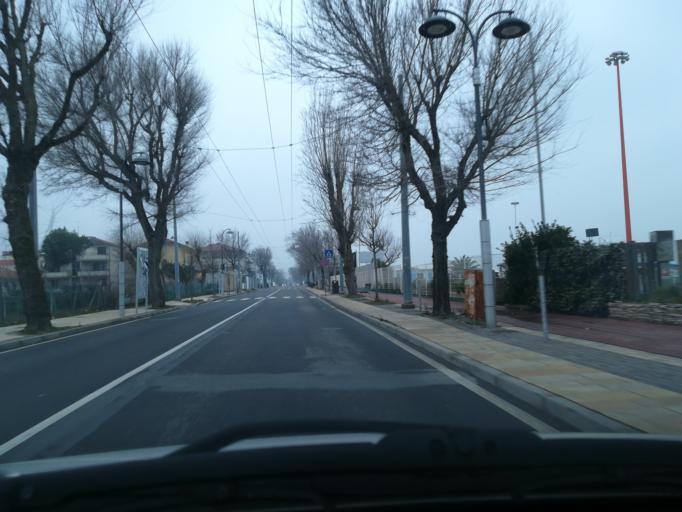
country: IT
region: Emilia-Romagna
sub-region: Provincia di Rimini
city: Riccione
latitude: 44.0188
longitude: 12.6381
